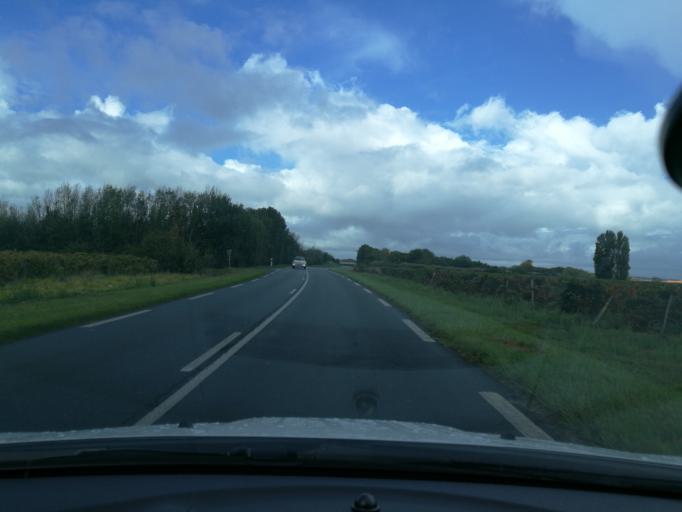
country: FR
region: Poitou-Charentes
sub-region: Departement de la Charente-Maritime
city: Le Bois-Plage-en-Re
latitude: 46.2006
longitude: -1.3965
